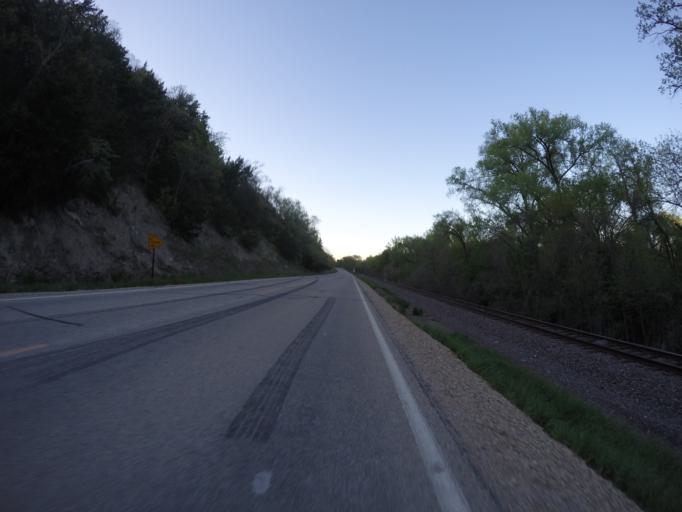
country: US
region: Kansas
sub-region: Riley County
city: Manhattan
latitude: 39.1590
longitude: -96.5963
